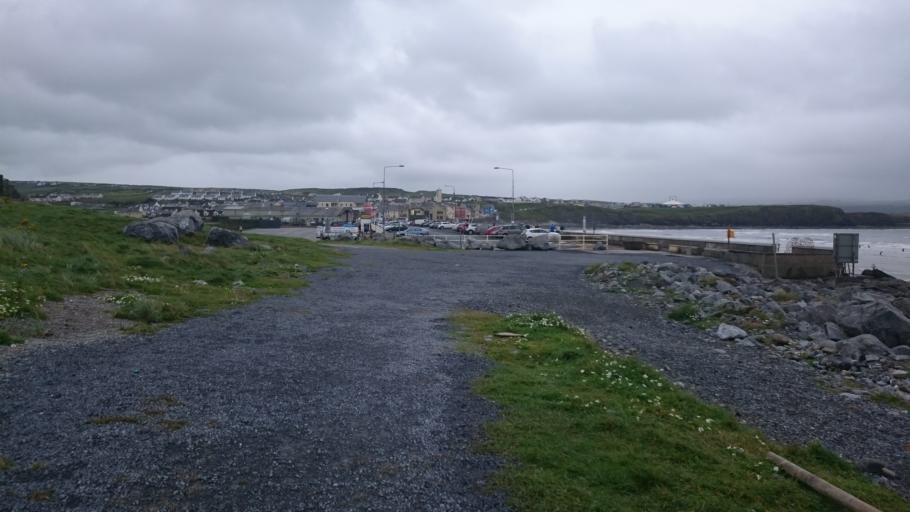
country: IE
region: Munster
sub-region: An Clar
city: Kilrush
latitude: 52.9358
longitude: -9.3508
